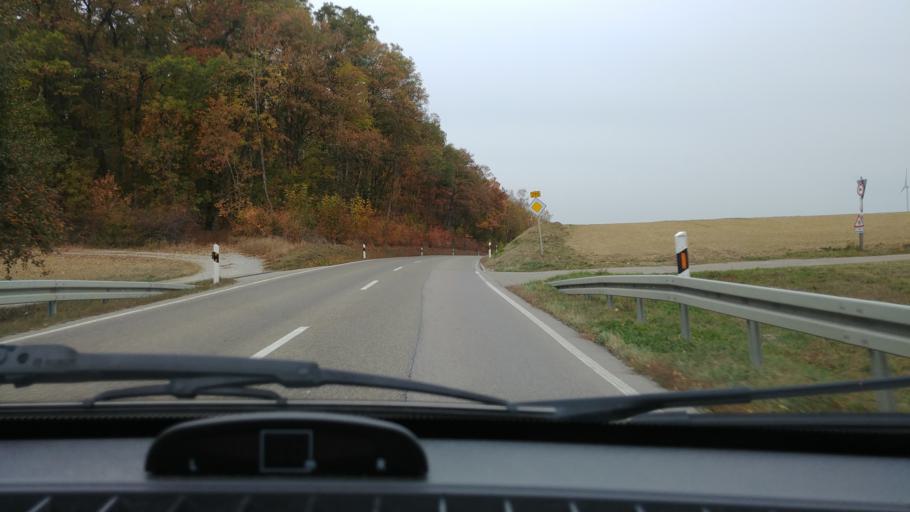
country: DE
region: Baden-Wuerttemberg
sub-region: Regierungsbezirk Stuttgart
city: Wallhausen
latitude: 49.2196
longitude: 10.0571
